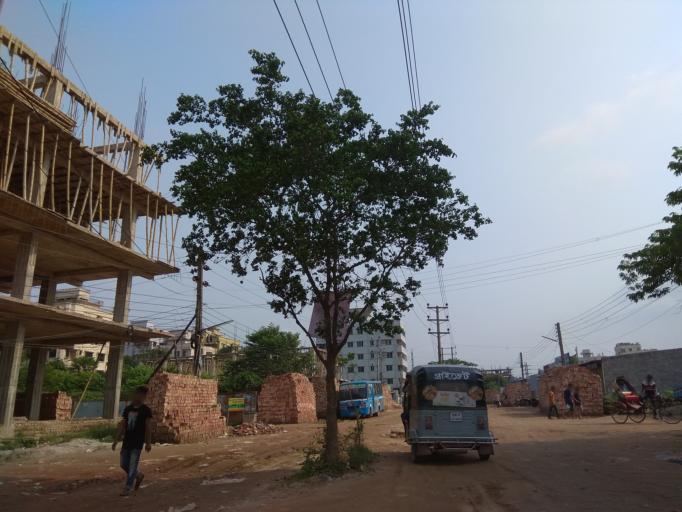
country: BD
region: Dhaka
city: Tungi
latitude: 23.8262
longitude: 90.3533
